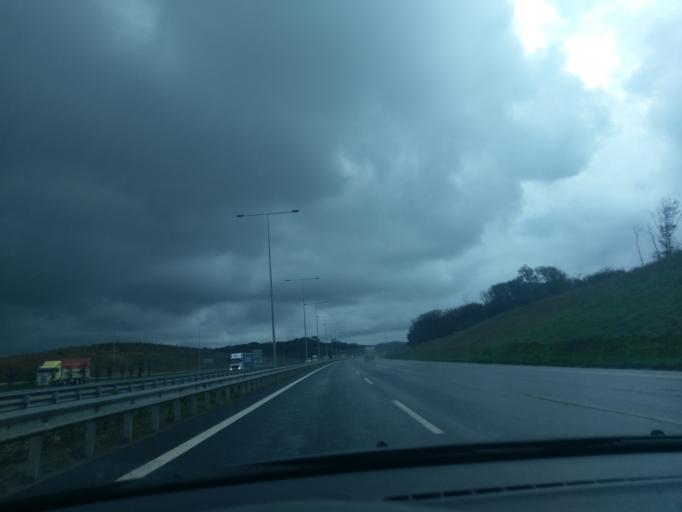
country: TR
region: Istanbul
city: Kemerburgaz
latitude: 41.2351
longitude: 28.9095
